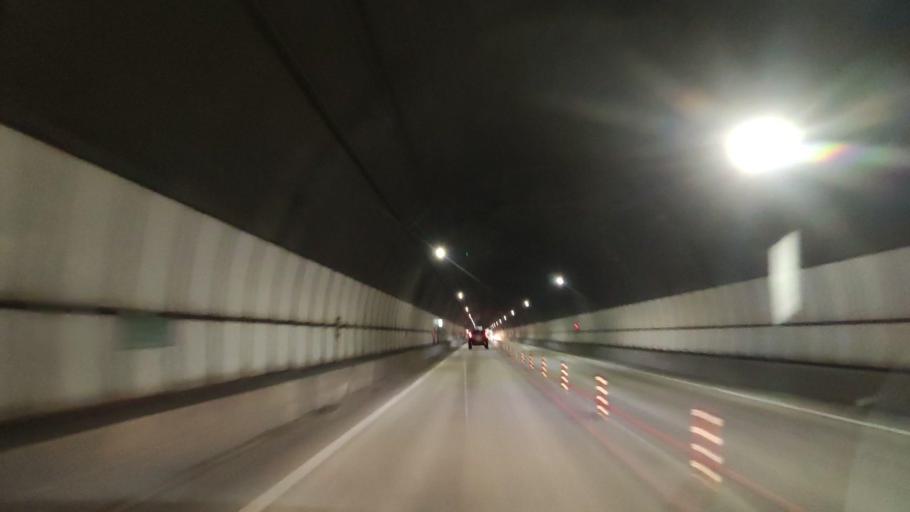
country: JP
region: Yamagata
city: Shinjo
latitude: 38.6863
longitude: 140.3148
